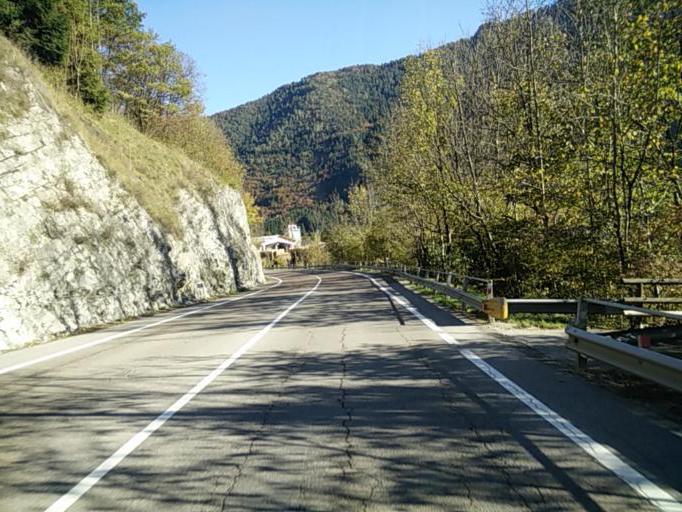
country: IT
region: Trentino-Alto Adige
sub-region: Provincia di Trento
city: Pieve di Ledro
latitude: 45.8923
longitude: 10.6942
